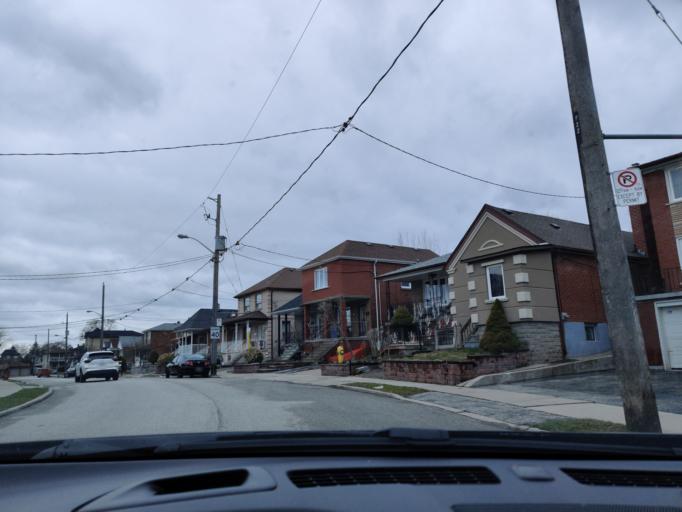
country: CA
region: Ontario
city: Toronto
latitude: 43.6900
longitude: -79.4504
